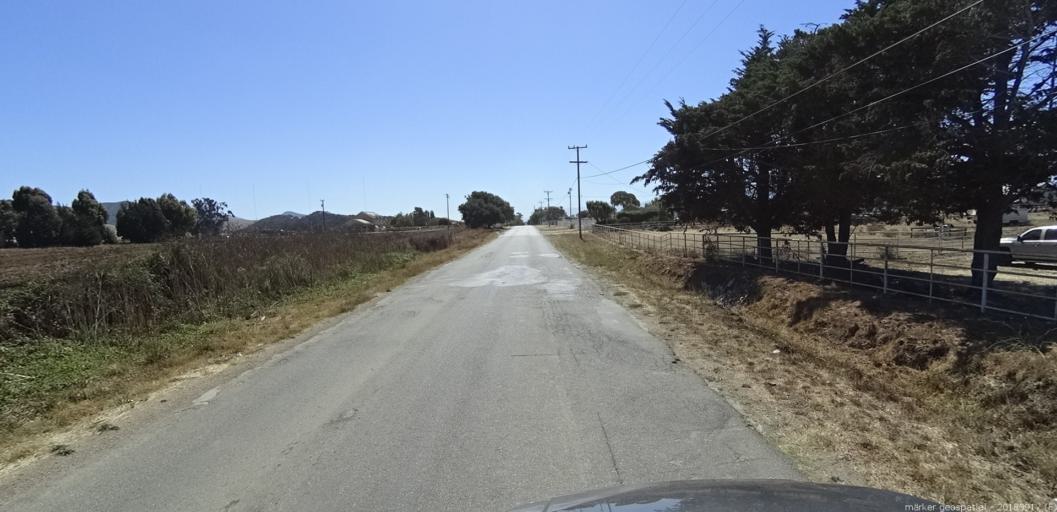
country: US
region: California
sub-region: Monterey County
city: Prunedale
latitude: 36.7374
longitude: -121.5999
